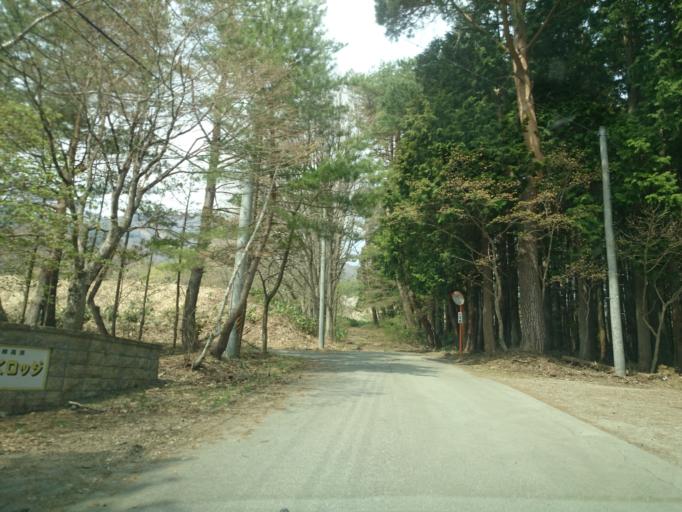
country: JP
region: Fukushima
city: Inawashiro
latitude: 37.5744
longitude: 140.1006
